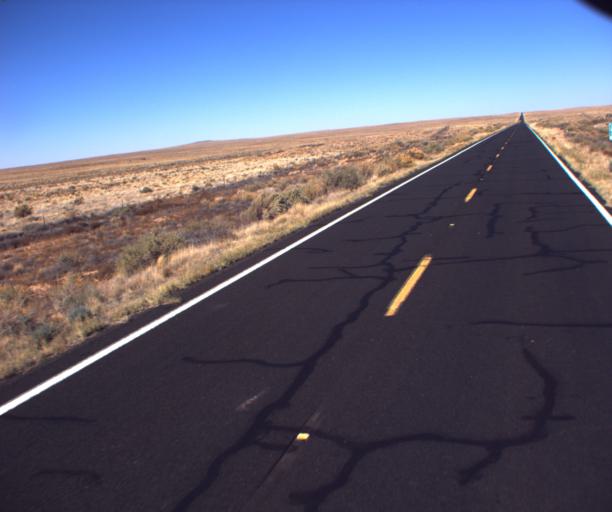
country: US
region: Arizona
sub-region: Navajo County
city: Dilkon
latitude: 35.5846
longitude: -110.4652
